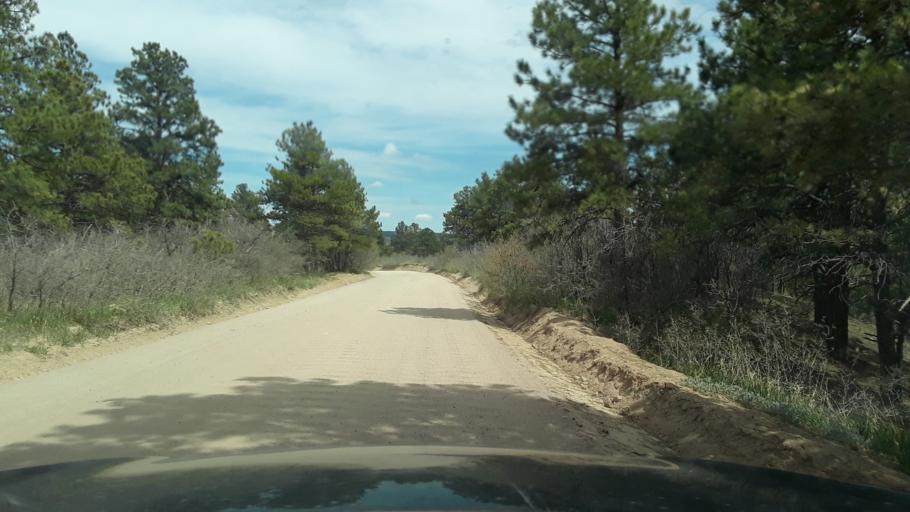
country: US
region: Colorado
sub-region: El Paso County
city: Monument
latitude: 39.0902
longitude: -104.9008
